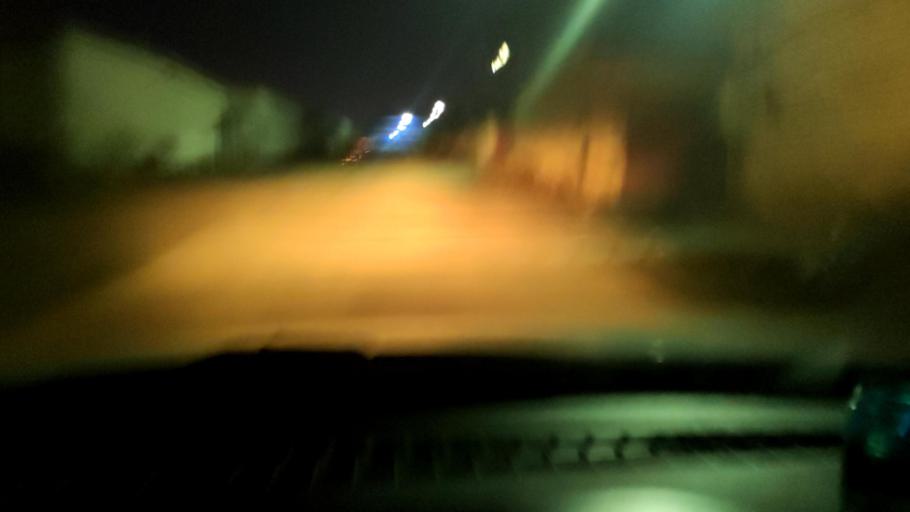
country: RU
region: Voronezj
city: Voronezh
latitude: 51.6363
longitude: 39.1291
